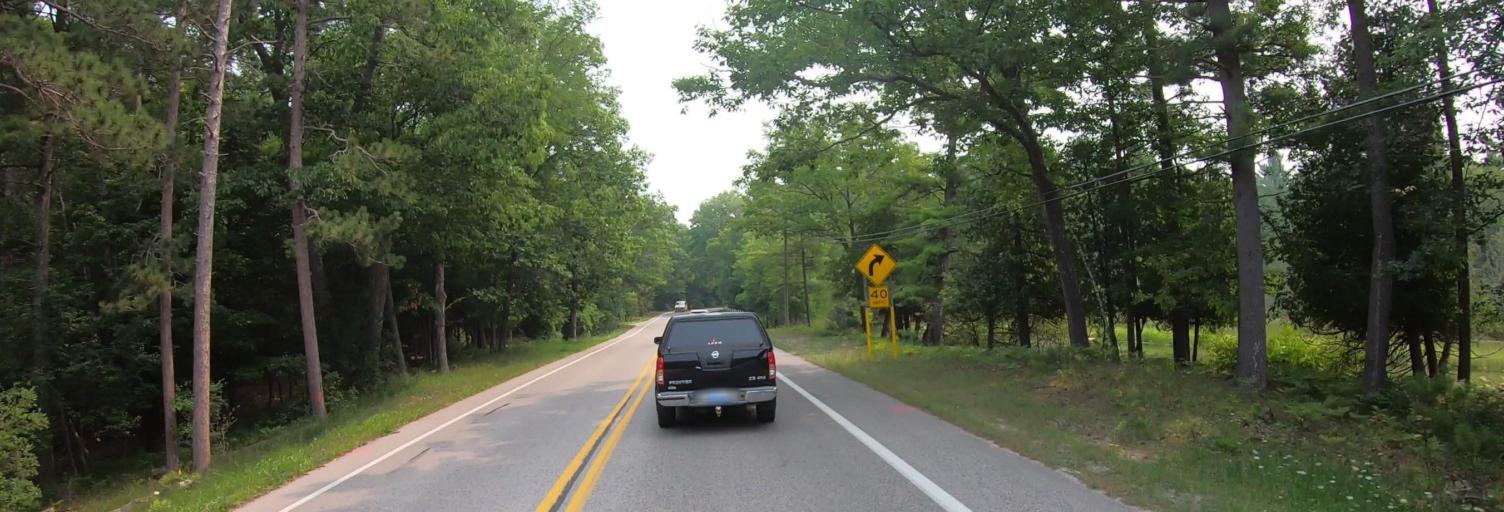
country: US
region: Michigan
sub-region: Leelanau County
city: Leland
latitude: 44.9088
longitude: -85.9702
